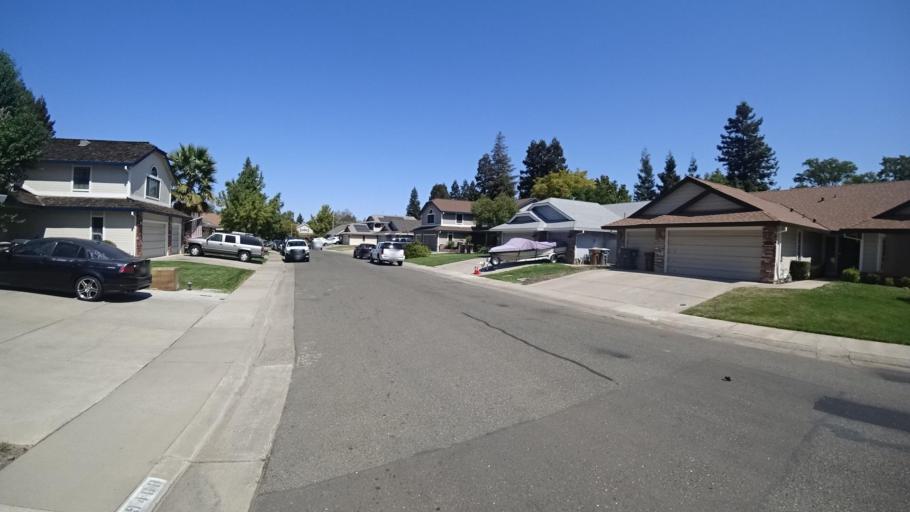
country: US
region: California
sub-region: Sacramento County
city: Laguna
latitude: 38.4135
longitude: -121.4159
